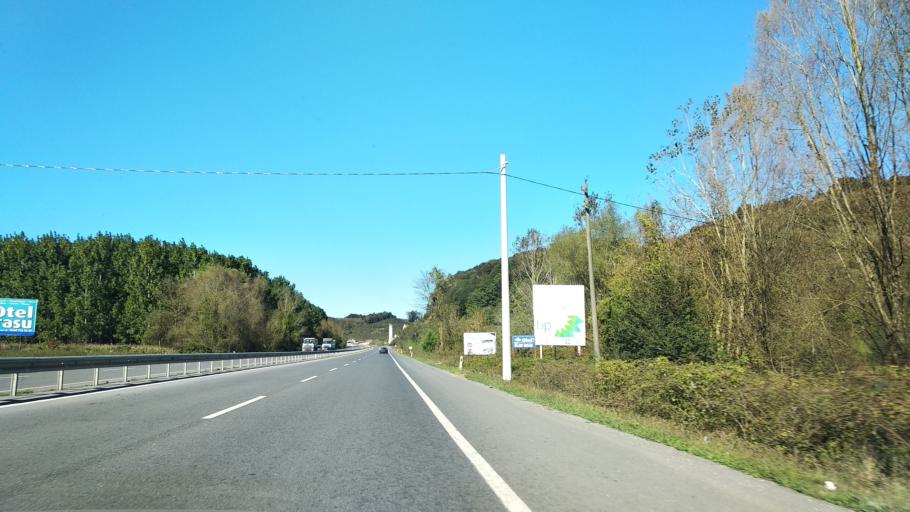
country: TR
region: Sakarya
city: Karasu
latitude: 41.0694
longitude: 30.6446
